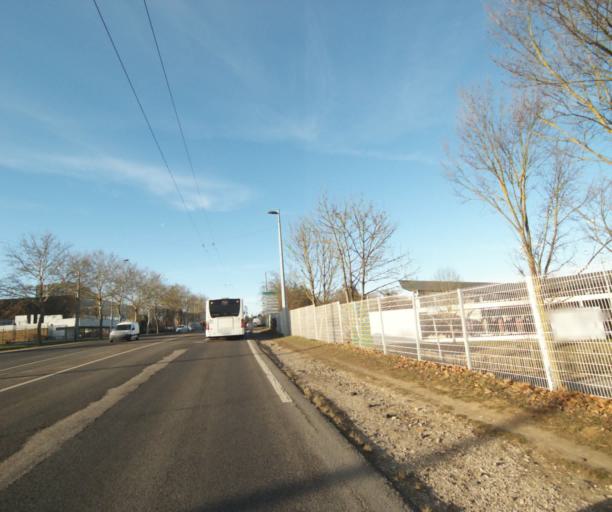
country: FR
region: Lorraine
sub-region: Departement de Meurthe-et-Moselle
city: Villers-les-Nancy
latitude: 48.6516
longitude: 6.1497
